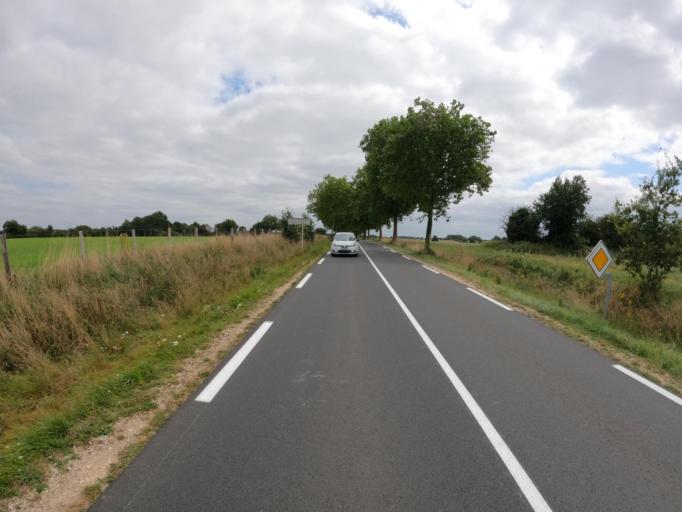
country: FR
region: Poitou-Charentes
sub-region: Departement de la Vienne
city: Charroux
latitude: 46.1384
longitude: 0.4375
